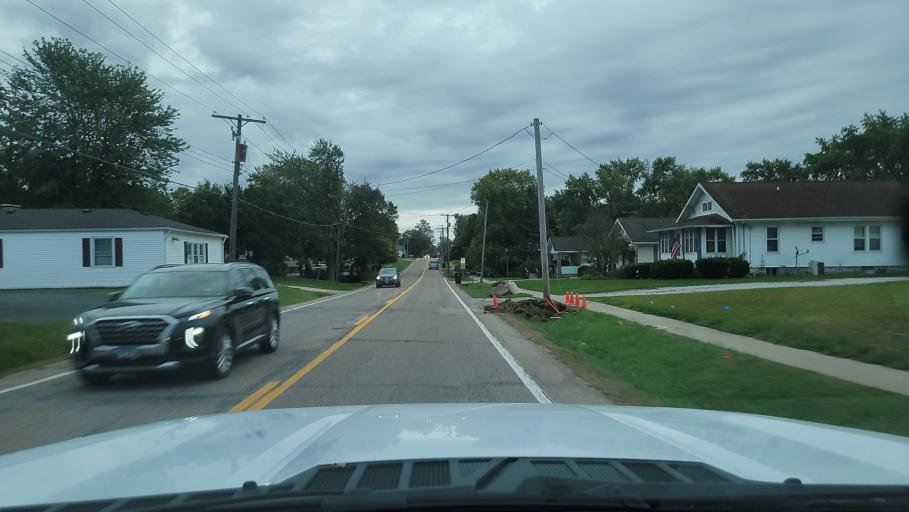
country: US
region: Illinois
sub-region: Schuyler County
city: Rushville
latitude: 40.1177
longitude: -90.5711
